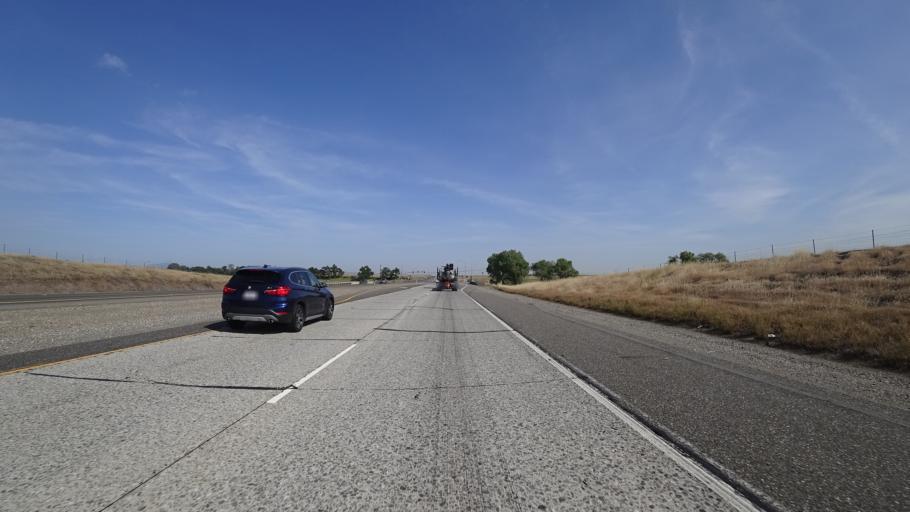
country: US
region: California
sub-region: Butte County
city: Durham
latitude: 39.6676
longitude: -121.7465
